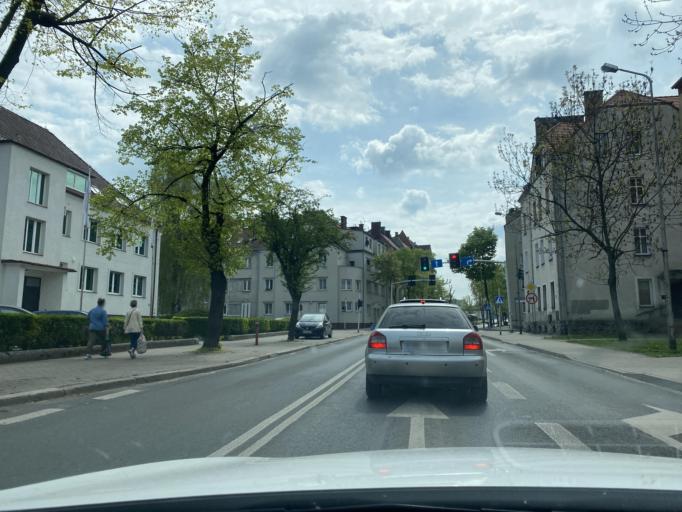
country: PL
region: Lower Silesian Voivodeship
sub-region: Powiat boleslawiecki
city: Boleslawiec
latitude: 51.2643
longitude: 15.5733
